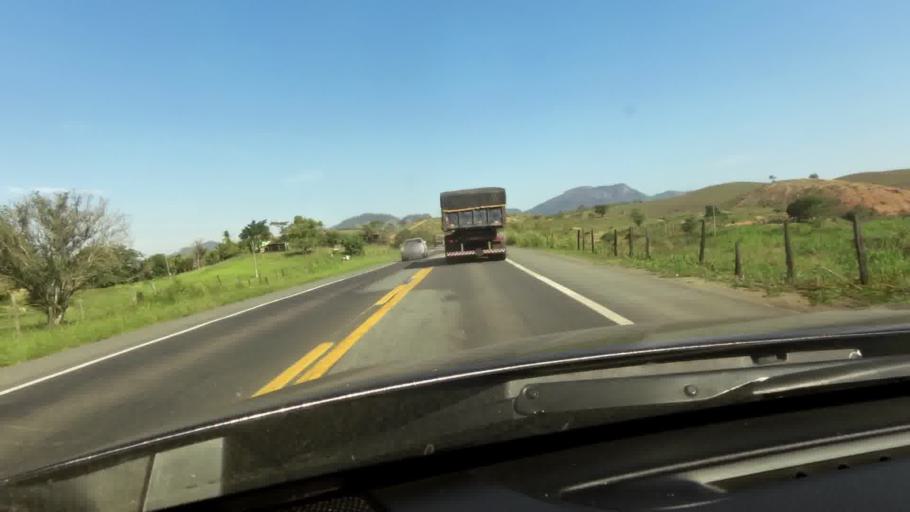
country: BR
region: Espirito Santo
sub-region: Cachoeiro De Itapemirim
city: Cachoeiro de Itapemirim
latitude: -20.9038
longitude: -41.0617
